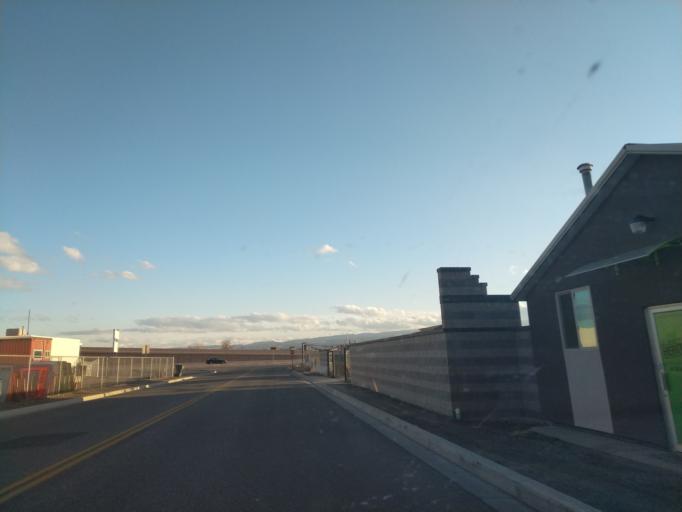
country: US
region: Colorado
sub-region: Mesa County
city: Fruitvale
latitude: 39.0736
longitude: -108.5174
